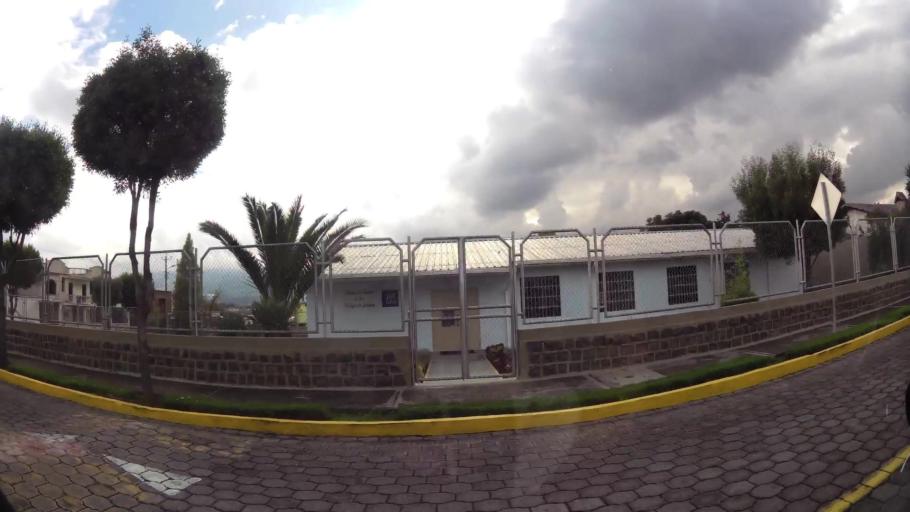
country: EC
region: Pichincha
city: Sangolqui
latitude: -0.3274
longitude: -78.4572
